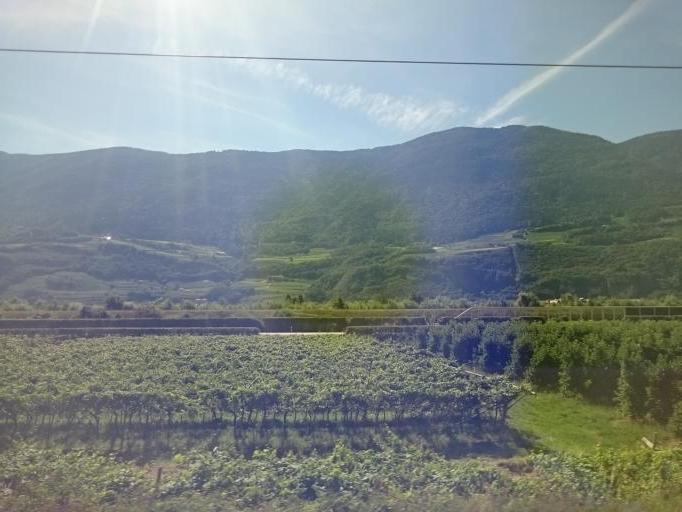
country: IT
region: Trentino-Alto Adige
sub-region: Bolzano
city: Salorno
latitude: 46.2493
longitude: 11.2102
